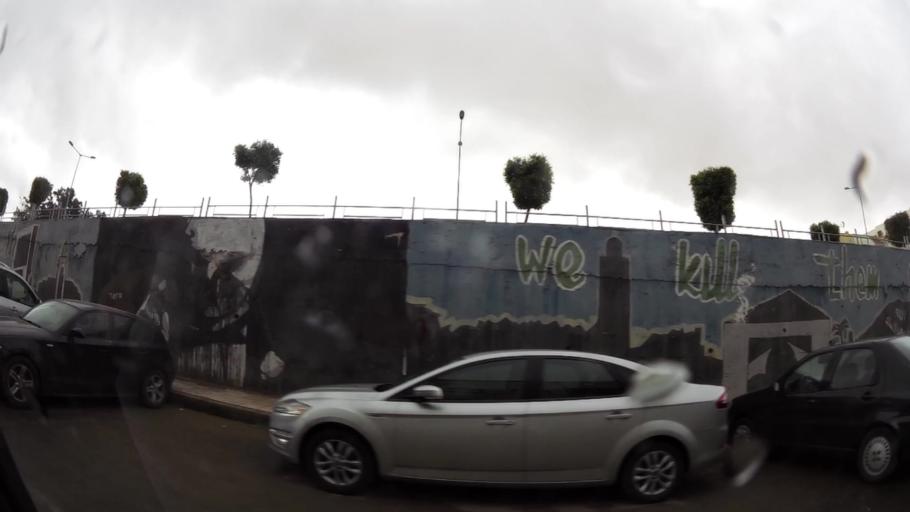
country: MA
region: Grand Casablanca
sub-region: Mediouna
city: Tit Mellil
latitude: 33.6191
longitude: -7.4847
